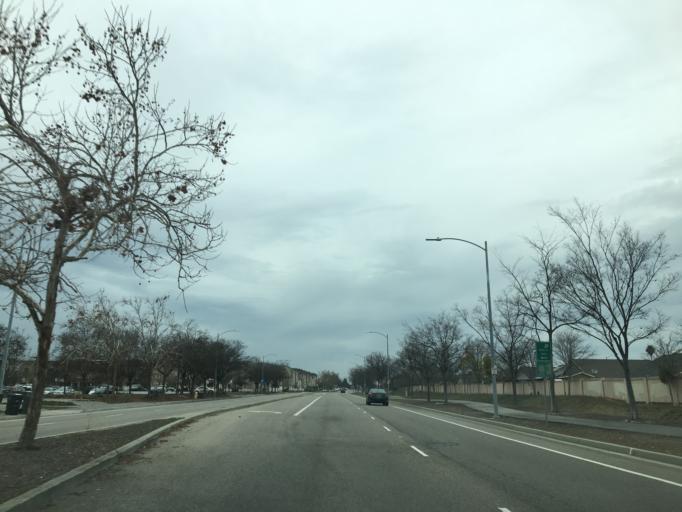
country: US
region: California
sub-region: Santa Clara County
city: Morgan Hill
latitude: 37.1299
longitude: -121.6481
